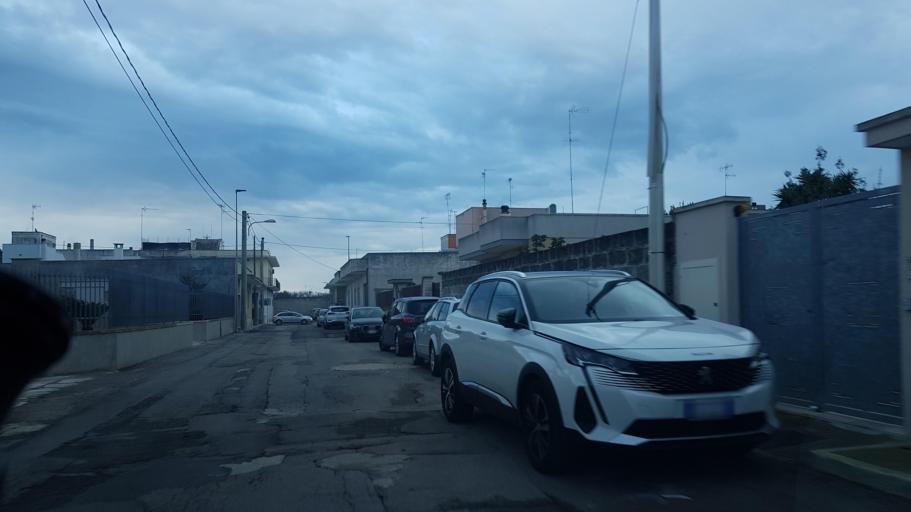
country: IT
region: Apulia
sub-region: Provincia di Lecce
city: Merine
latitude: 40.3362
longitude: 18.2204
